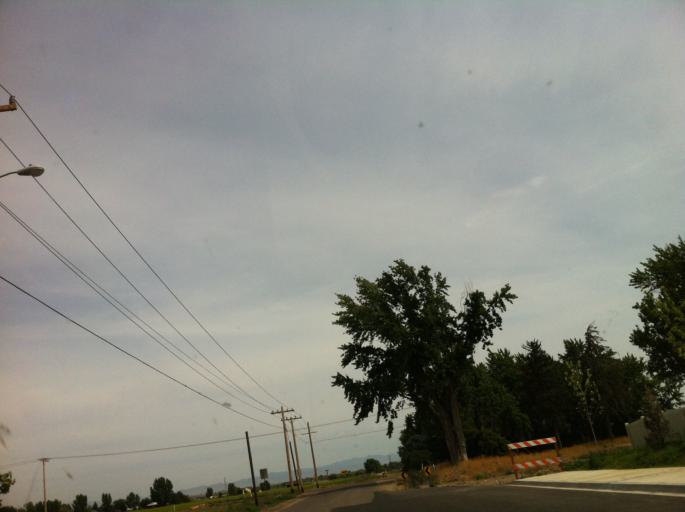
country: US
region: Idaho
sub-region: Payette County
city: Fruitland
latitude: 44.0318
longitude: -116.9336
